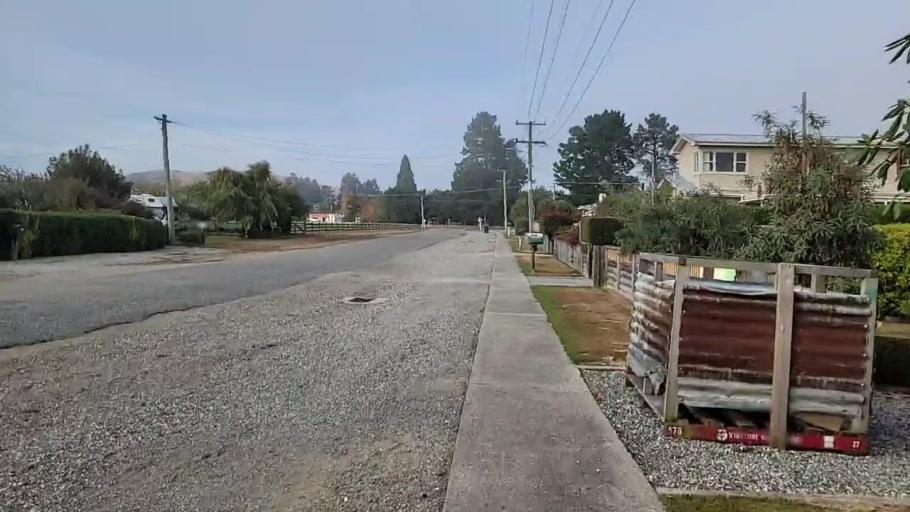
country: NZ
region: Southland
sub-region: Gore District
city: Gore
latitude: -45.6312
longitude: 169.3616
